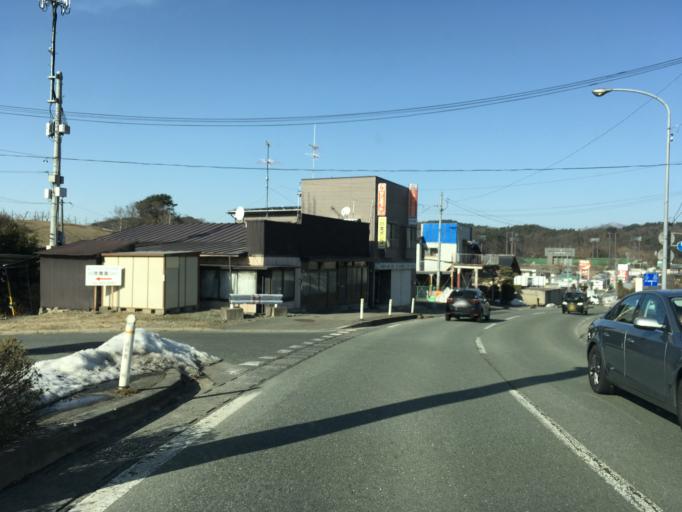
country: JP
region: Iwate
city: Morioka-shi
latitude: 39.7242
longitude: 141.1569
